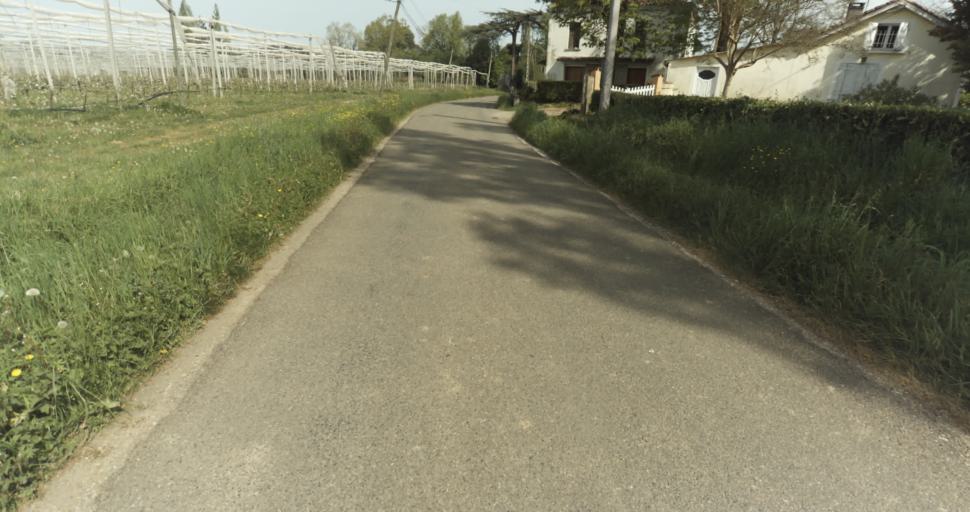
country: FR
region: Midi-Pyrenees
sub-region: Departement du Tarn-et-Garonne
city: Moissac
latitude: 44.0911
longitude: 1.0791
